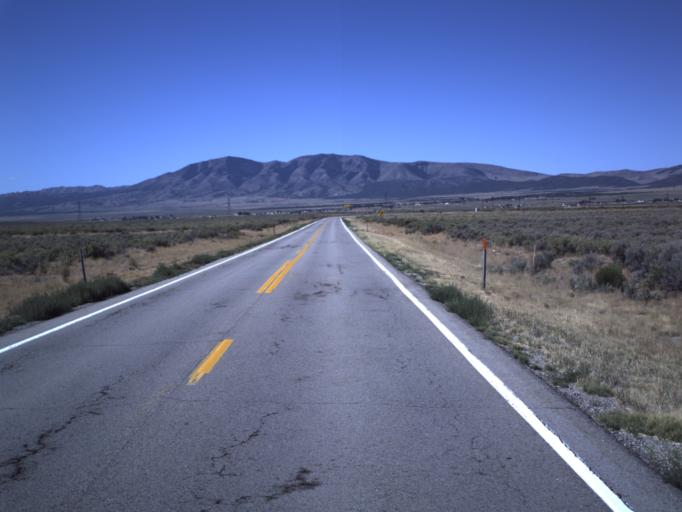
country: US
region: Utah
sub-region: Tooele County
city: Tooele
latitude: 40.3701
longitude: -112.4023
